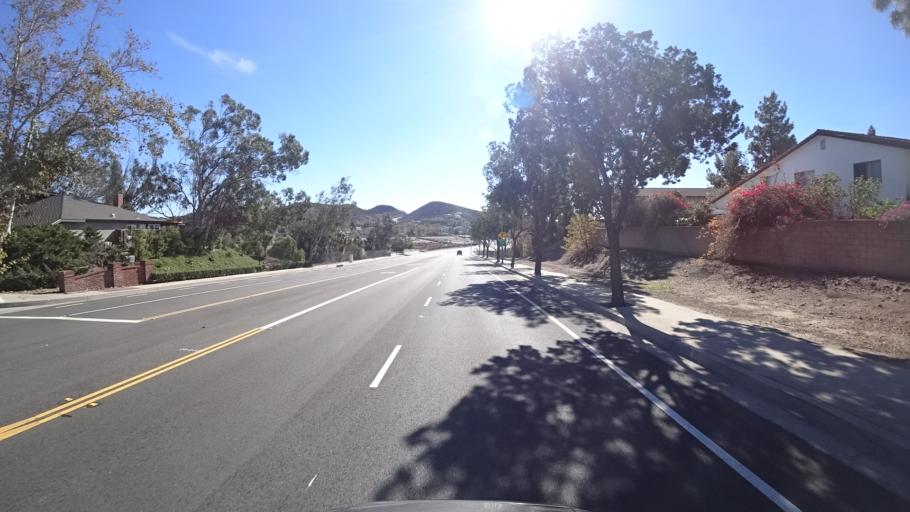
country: US
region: California
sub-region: Orange County
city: Villa Park
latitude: 33.8162
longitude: -117.7954
